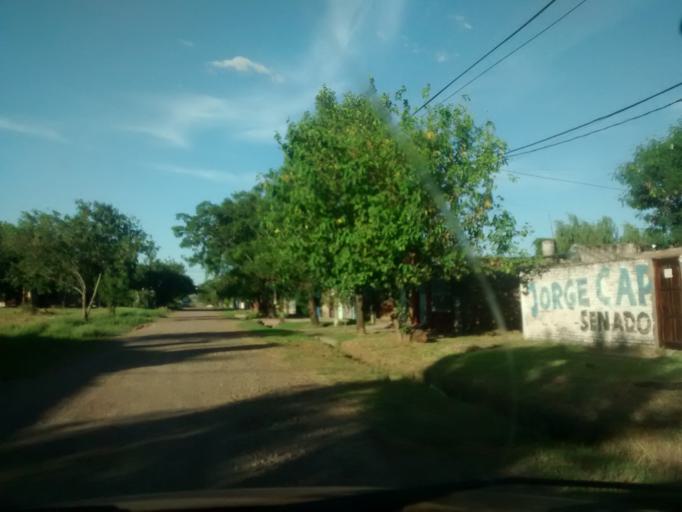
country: AR
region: Chaco
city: Fontana
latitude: -27.4542
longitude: -59.0235
